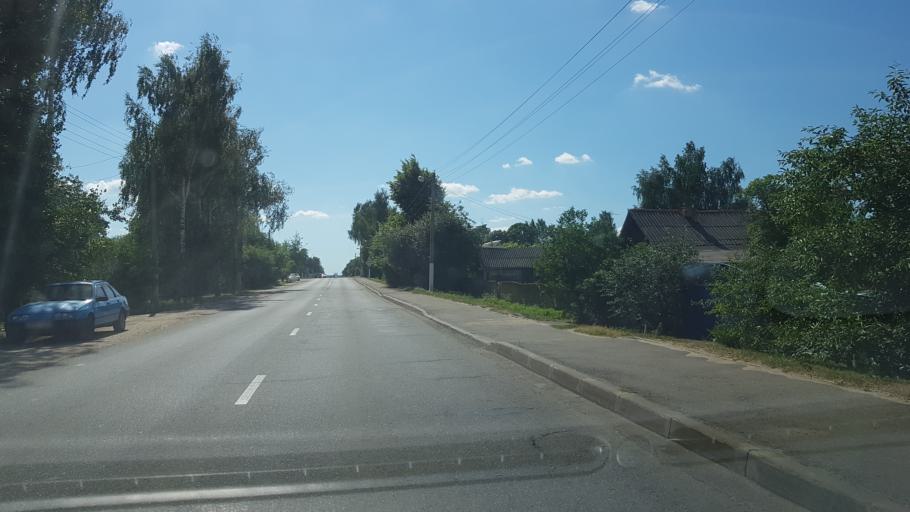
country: BY
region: Vitebsk
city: Orsha
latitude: 54.5060
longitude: 30.4446
